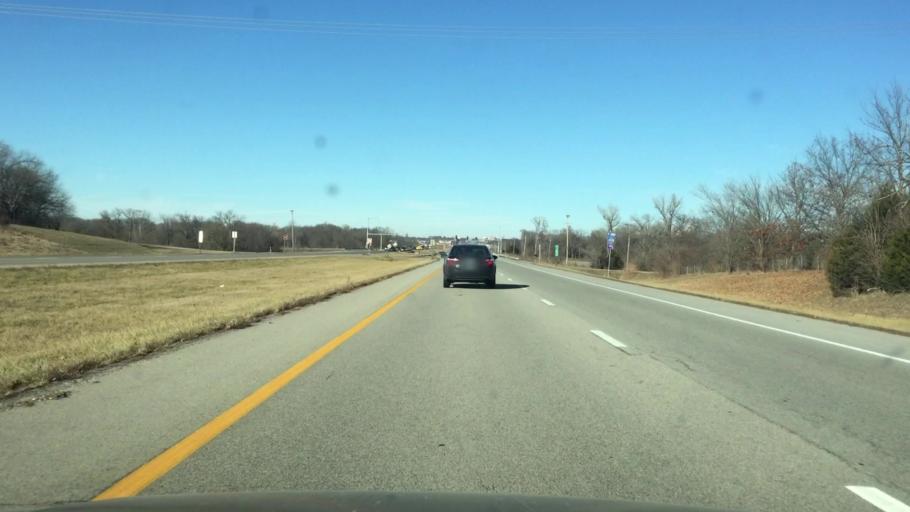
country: US
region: Kansas
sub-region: Douglas County
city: Lawrence
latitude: 38.9053
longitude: -95.2604
